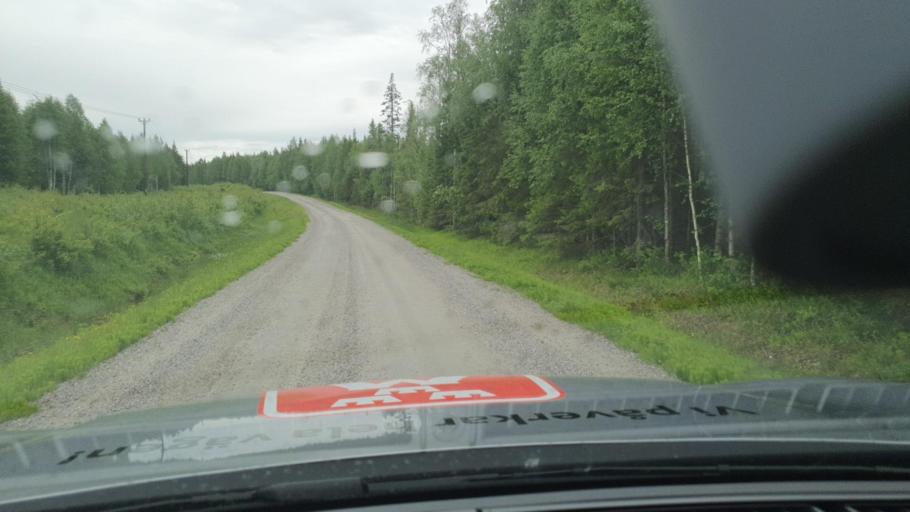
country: SE
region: Norrbotten
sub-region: Kalix Kommun
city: Rolfs
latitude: 66.0510
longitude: 23.0289
